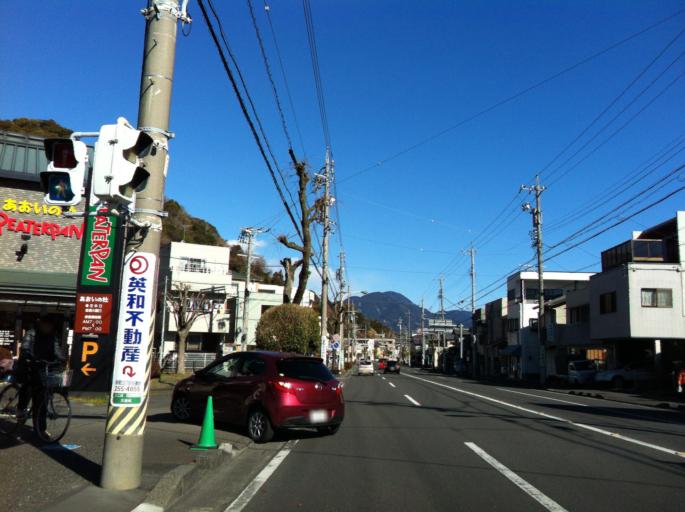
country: JP
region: Shizuoka
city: Shizuoka-shi
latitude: 34.9911
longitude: 138.3776
